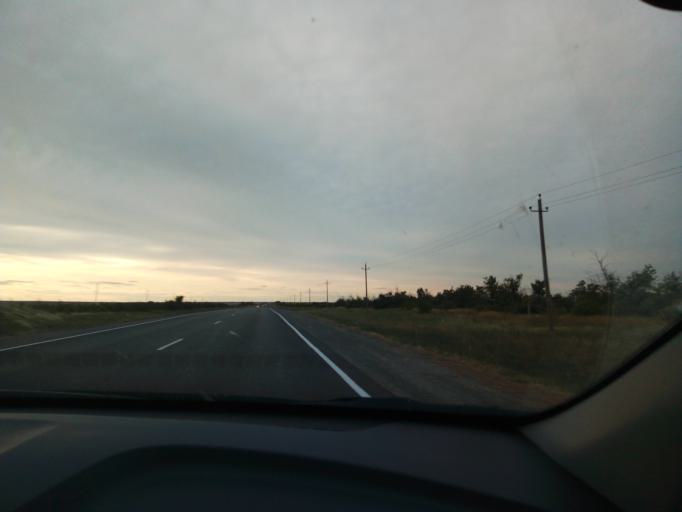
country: RU
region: Volgograd
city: Primorsk
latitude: 49.2396
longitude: 44.8955
